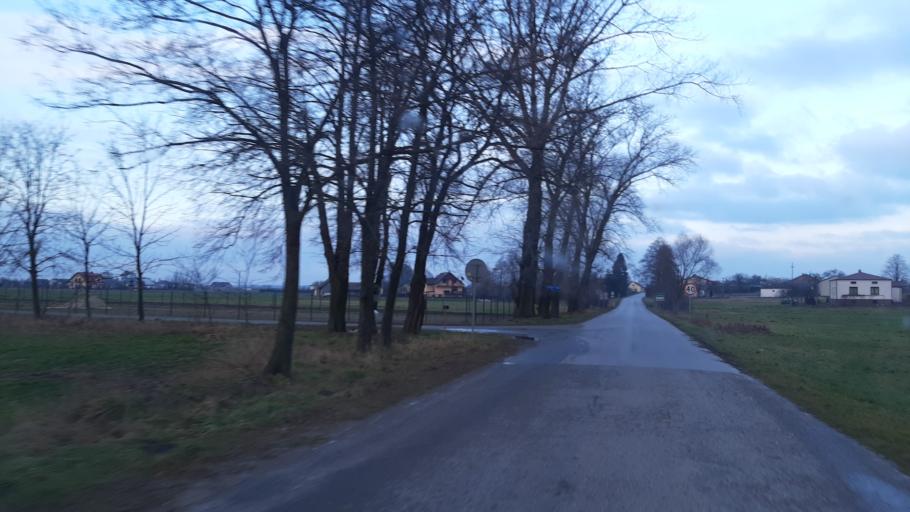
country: PL
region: Lublin Voivodeship
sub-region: Powiat lubartowski
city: Kamionka
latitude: 51.3993
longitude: 22.4115
